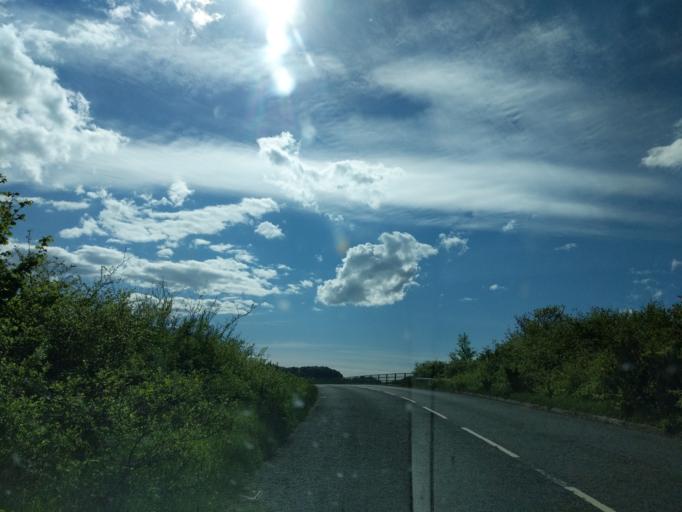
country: GB
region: Scotland
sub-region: Edinburgh
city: Ratho
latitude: 55.9306
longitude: -3.3634
